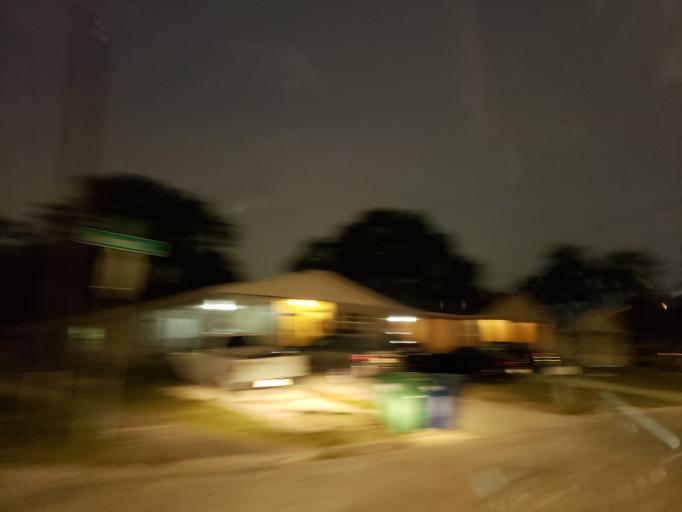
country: US
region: Florida
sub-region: Hillsborough County
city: University
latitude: 28.0283
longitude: -82.4367
